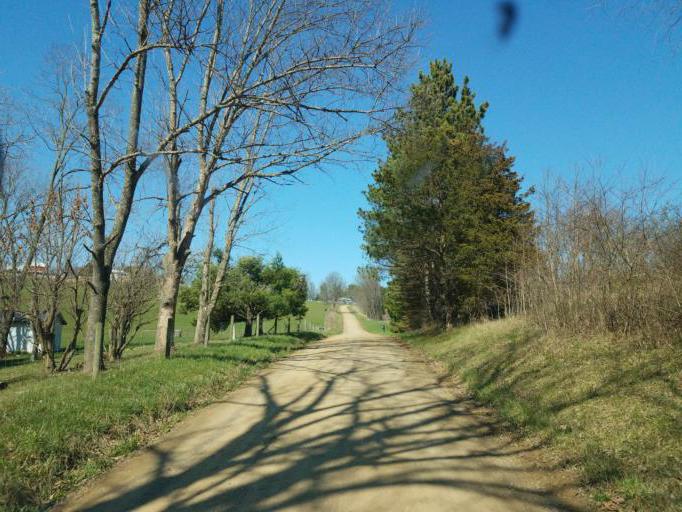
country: US
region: Ohio
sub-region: Knox County
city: Oak Hill
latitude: 40.4246
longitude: -82.2113
